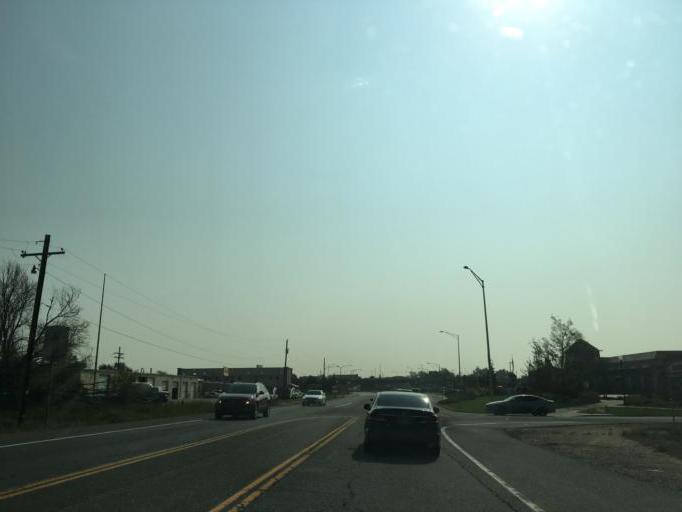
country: US
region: Colorado
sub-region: Adams County
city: Brighton
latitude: 39.9869
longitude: -104.8283
